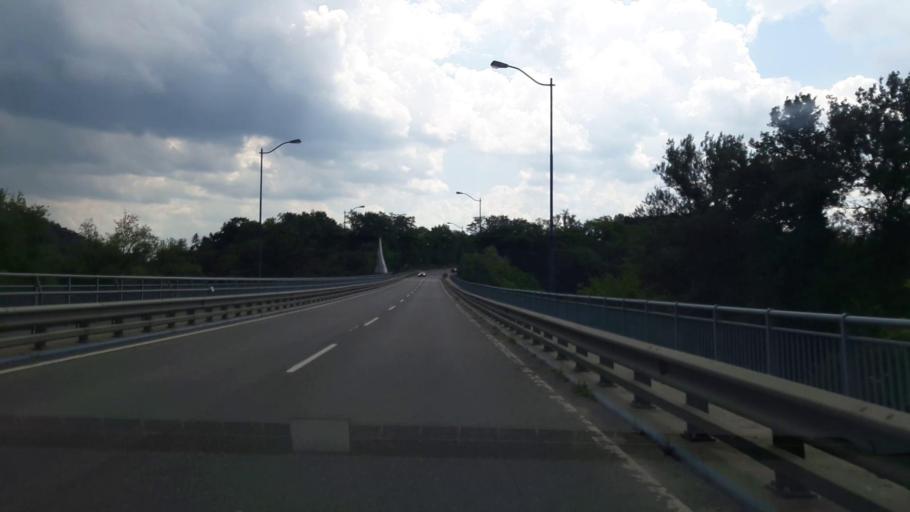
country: AT
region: Lower Austria
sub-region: Politischer Bezirk Melk
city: Emmersdorf an der Donau
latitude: 48.2408
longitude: 15.3468
